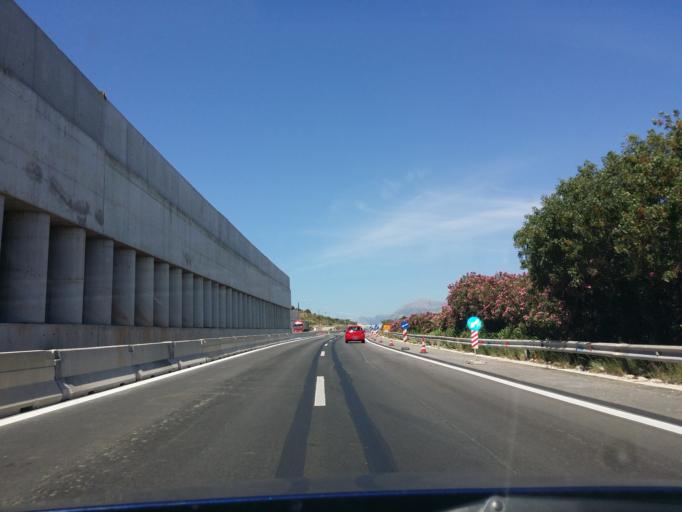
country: GR
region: West Greece
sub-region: Nomos Achaias
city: Ano Kastritsion
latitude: 38.3236
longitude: 21.8788
